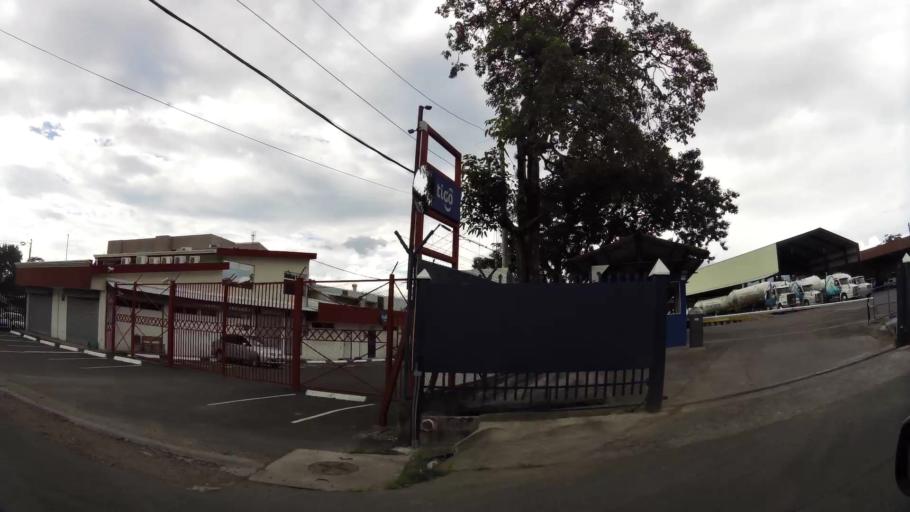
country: CR
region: Heredia
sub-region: Canton de Belen
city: San Antonio
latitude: 9.9617
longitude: -84.1924
